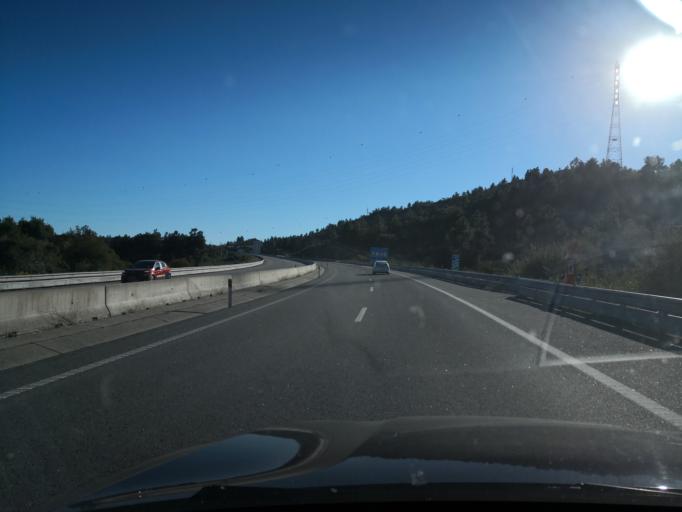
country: PT
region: Vila Real
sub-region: Sabrosa
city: Sabrosa
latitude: 41.3379
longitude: -7.6218
